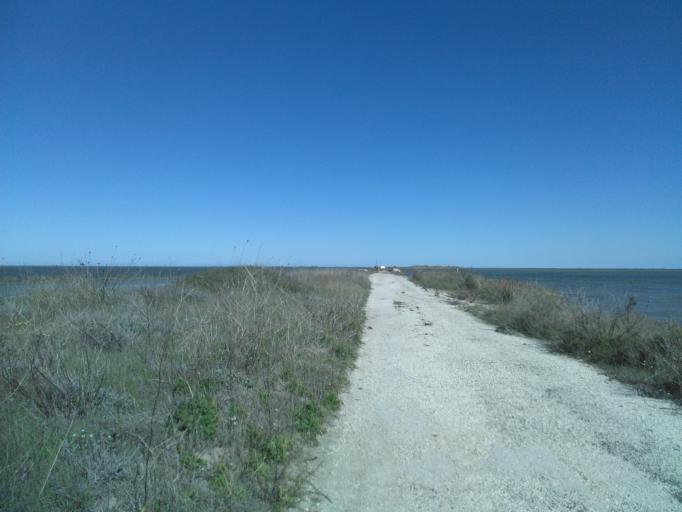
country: FR
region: Provence-Alpes-Cote d'Azur
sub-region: Departement des Bouches-du-Rhone
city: Saintes-Maries-de-la-Mer
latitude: 43.4154
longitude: 4.6135
